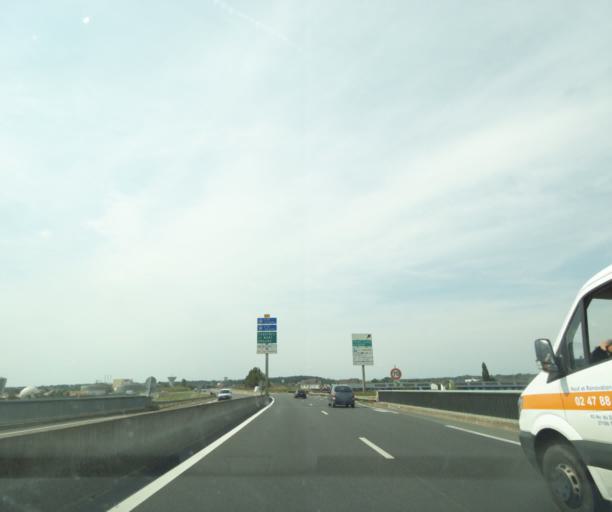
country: FR
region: Centre
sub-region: Departement d'Indre-et-Loire
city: La Riche
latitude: 47.3751
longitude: 0.6522
